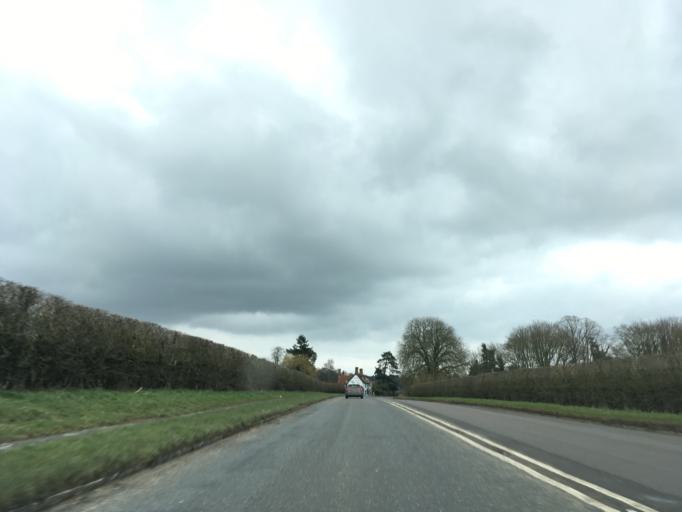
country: GB
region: England
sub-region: West Berkshire
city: Kintbury
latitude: 51.4128
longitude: -1.4185
